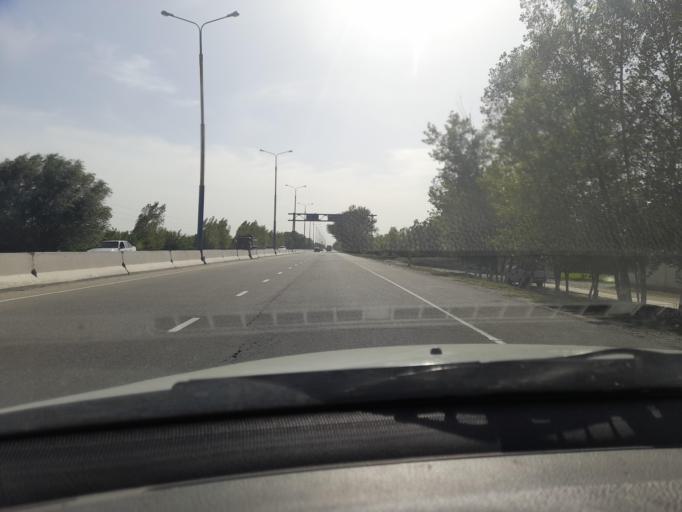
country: UZ
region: Samarqand
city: Ishtixon
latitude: 39.9491
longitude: 66.4235
